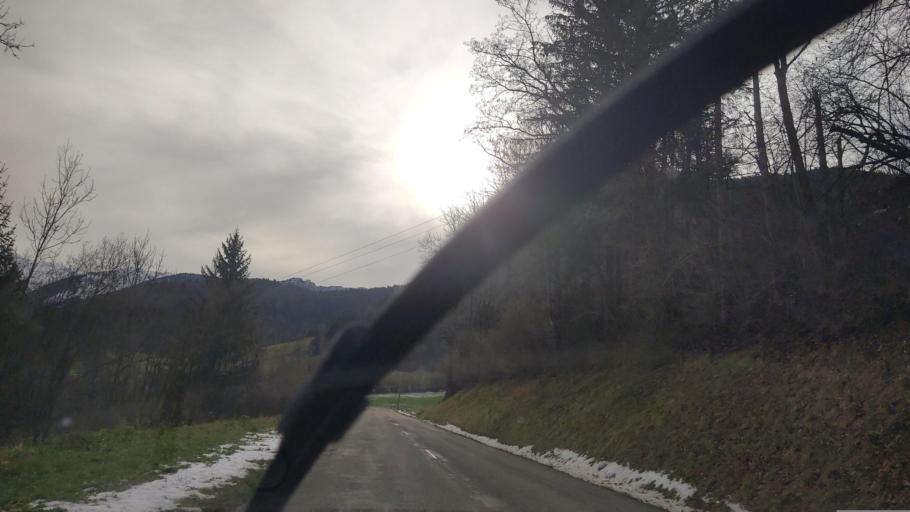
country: FR
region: Rhone-Alpes
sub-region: Departement de la Haute-Savoie
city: Doussard
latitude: 45.6723
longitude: 6.1450
